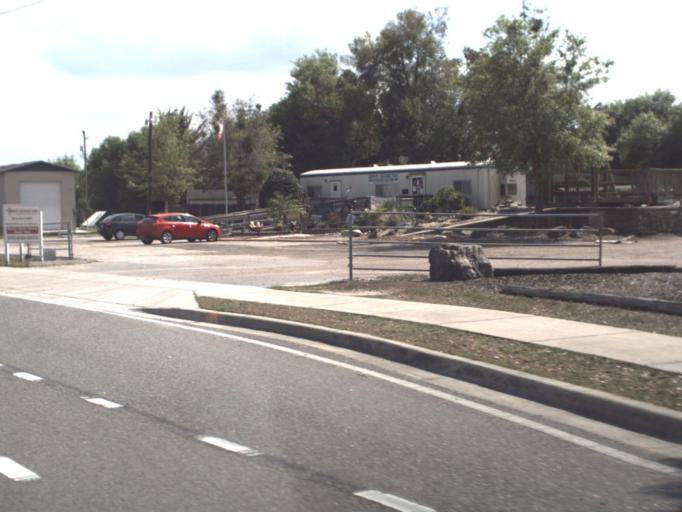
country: US
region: Florida
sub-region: Lake County
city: Minneola
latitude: 28.5768
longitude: -81.7491
